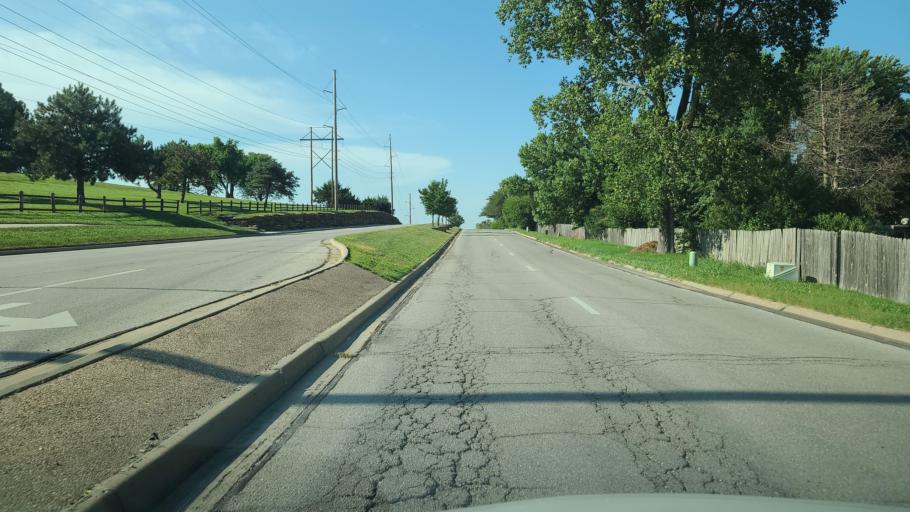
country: US
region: Kansas
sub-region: Douglas County
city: Lawrence
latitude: 38.9828
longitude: -95.2789
